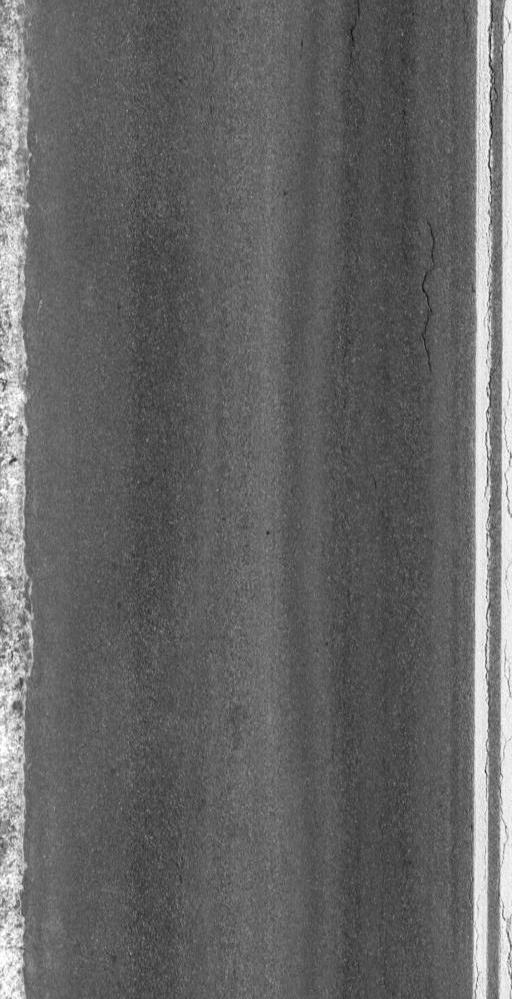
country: US
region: Vermont
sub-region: Chittenden County
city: Burlington
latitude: 44.3634
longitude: -73.2229
